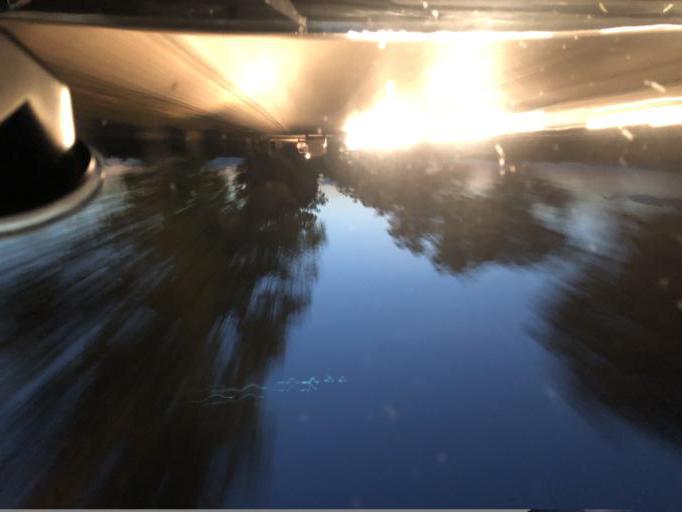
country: TN
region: Al Qasrayn
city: Kasserine
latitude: 35.2614
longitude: 9.0440
